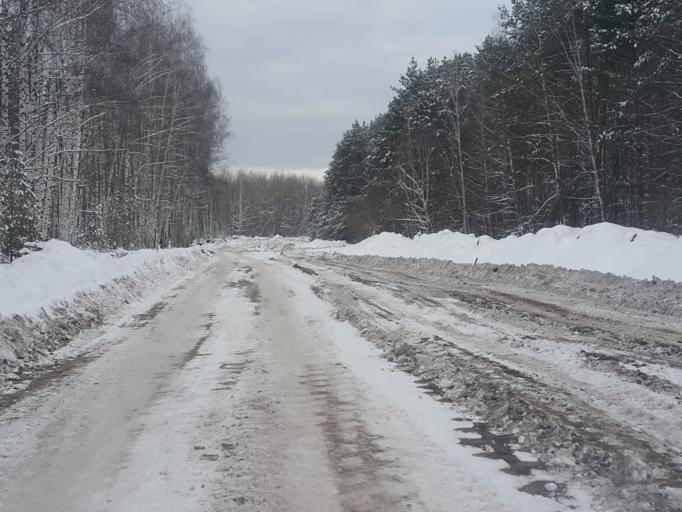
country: RU
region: Tambov
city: Platonovka
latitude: 52.8845
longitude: 41.8610
